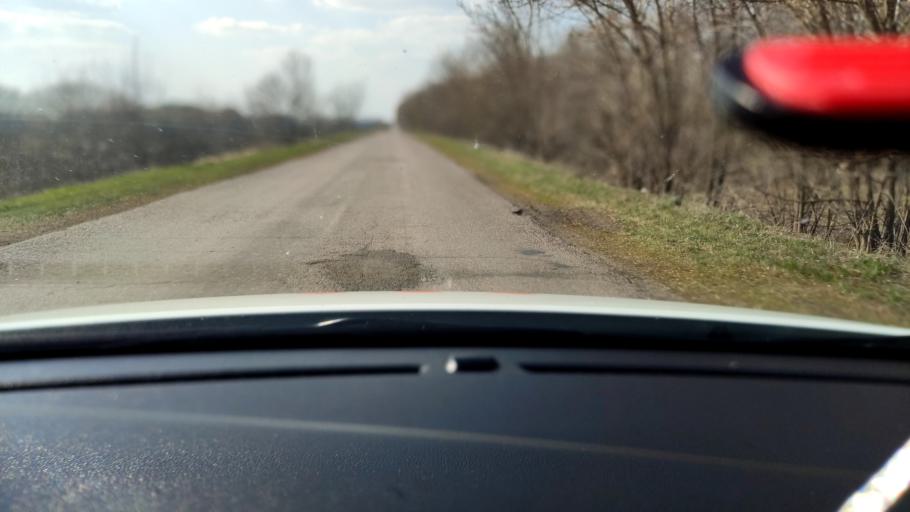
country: RU
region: Voronezj
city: Uryv-Pokrovka
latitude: 51.1222
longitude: 39.1266
